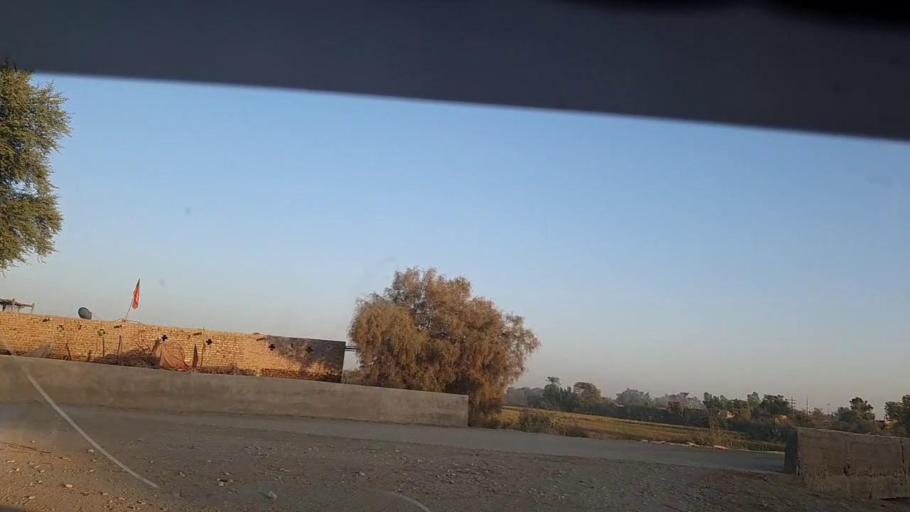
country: PK
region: Sindh
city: Ratodero
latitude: 27.9038
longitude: 68.2402
